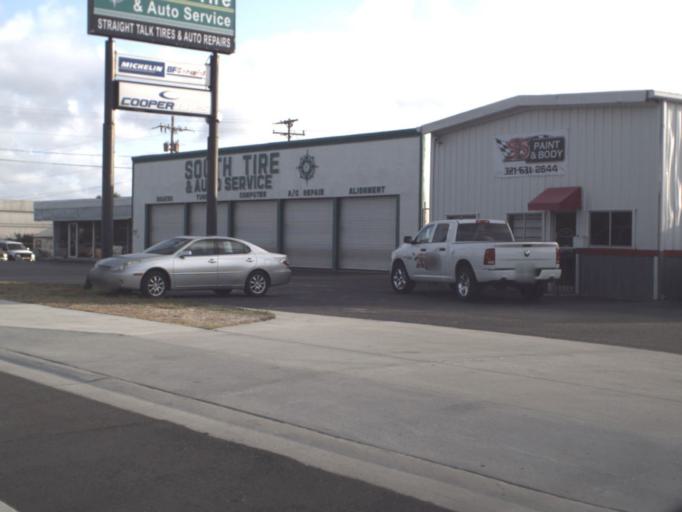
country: US
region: Florida
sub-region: Brevard County
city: Rockledge
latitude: 28.3655
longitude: -80.7357
